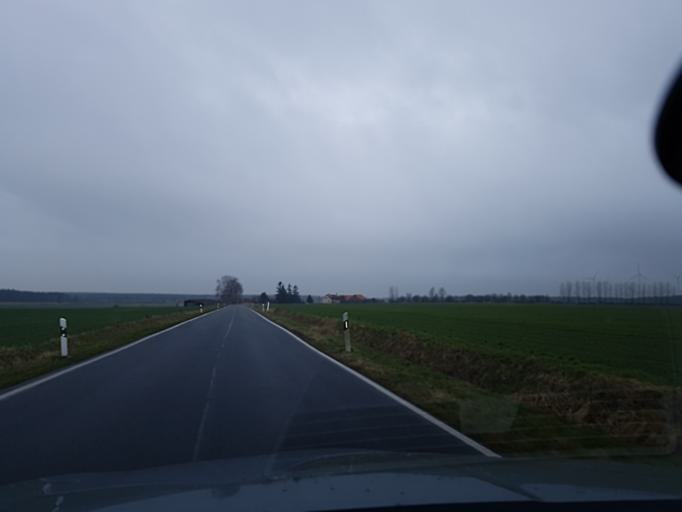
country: DE
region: Brandenburg
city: Trobitz
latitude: 51.6565
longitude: 13.4164
